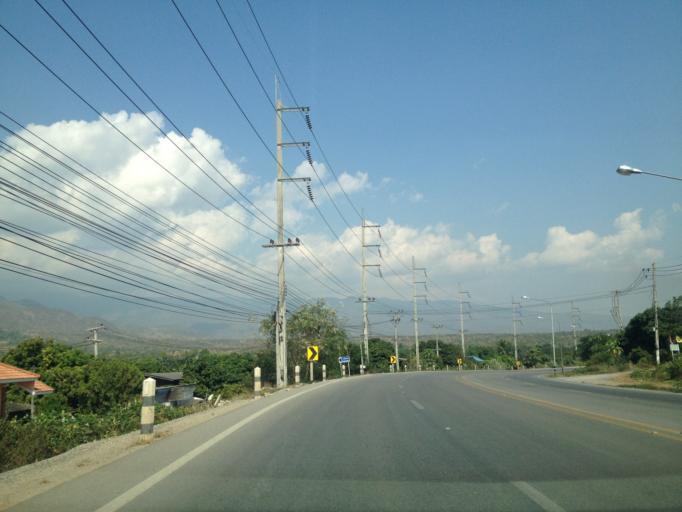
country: TH
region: Chiang Mai
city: Hot
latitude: 18.2476
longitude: 98.6047
